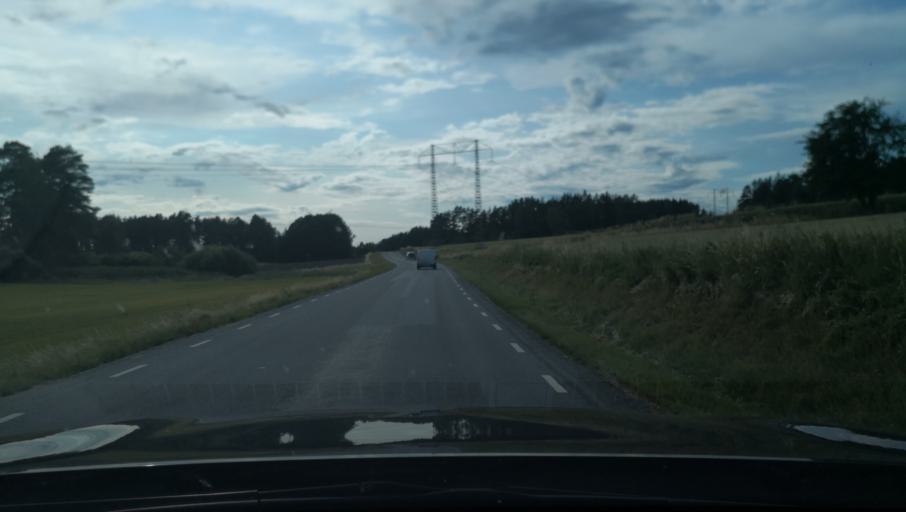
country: SE
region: Uppsala
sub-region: Enkopings Kommun
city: Orsundsbro
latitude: 59.6745
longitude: 17.4271
